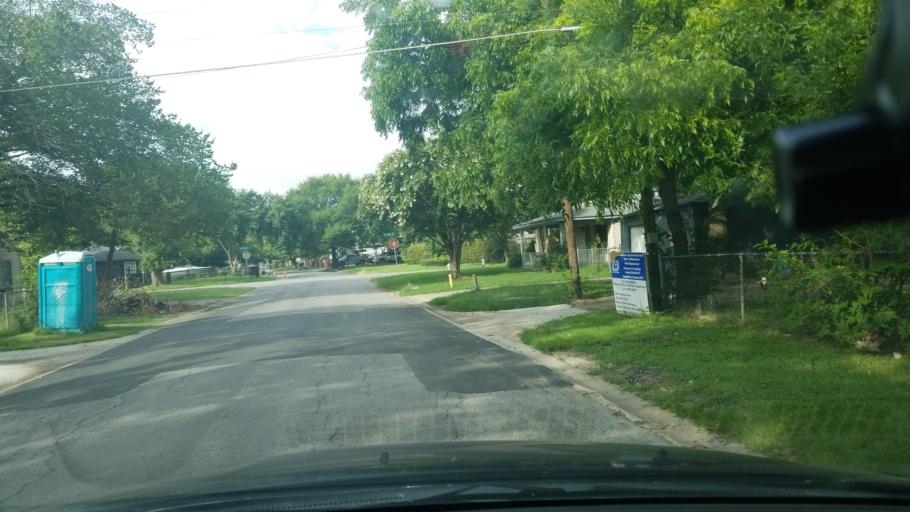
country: US
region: Texas
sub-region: Dallas County
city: Balch Springs
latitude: 32.7361
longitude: -96.6708
